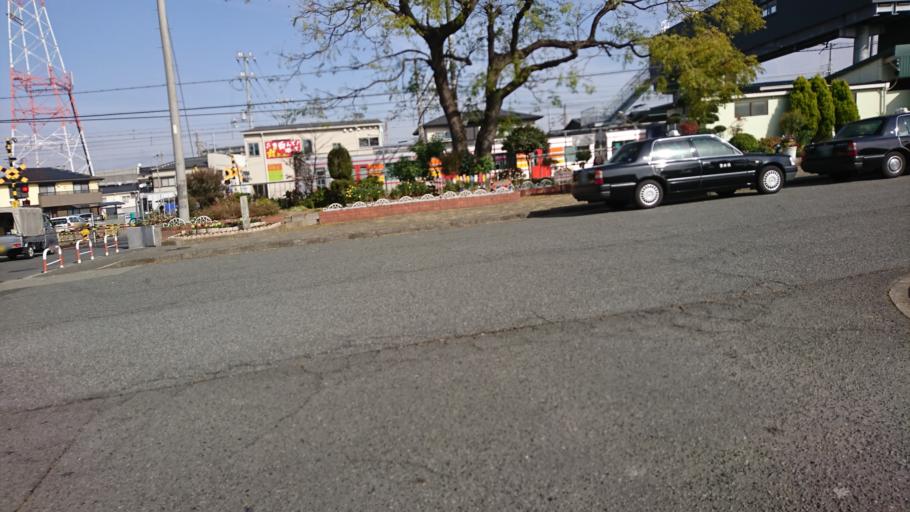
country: JP
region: Hyogo
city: Kakogawacho-honmachi
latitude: 34.7409
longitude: 134.8334
